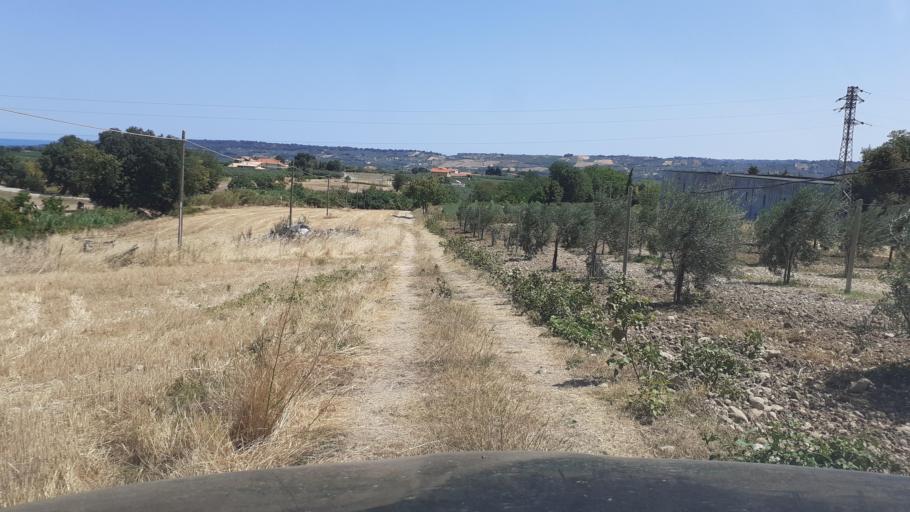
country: IT
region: Abruzzo
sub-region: Provincia di Chieti
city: Santa Maria Imbaro
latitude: 42.2141
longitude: 14.4626
